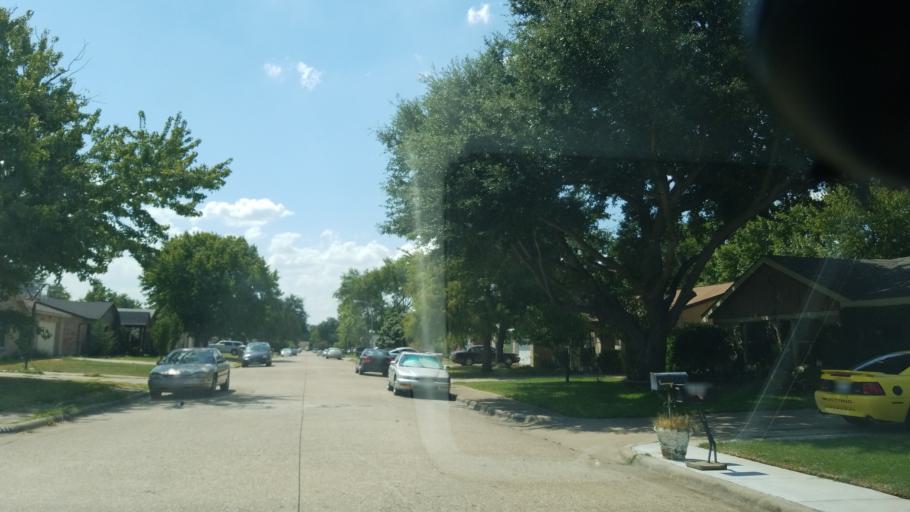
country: US
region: Texas
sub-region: Dallas County
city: Grand Prairie
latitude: 32.7149
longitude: -96.9904
